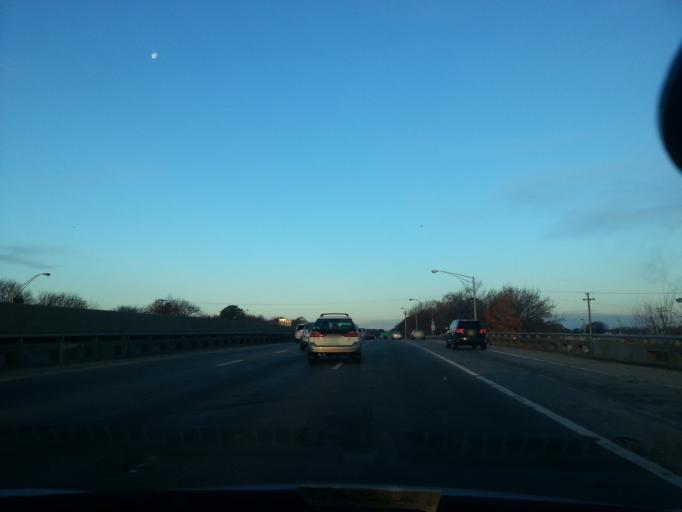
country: US
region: Virginia
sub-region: City of Norfolk
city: Norfolk
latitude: 36.8819
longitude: -76.2137
